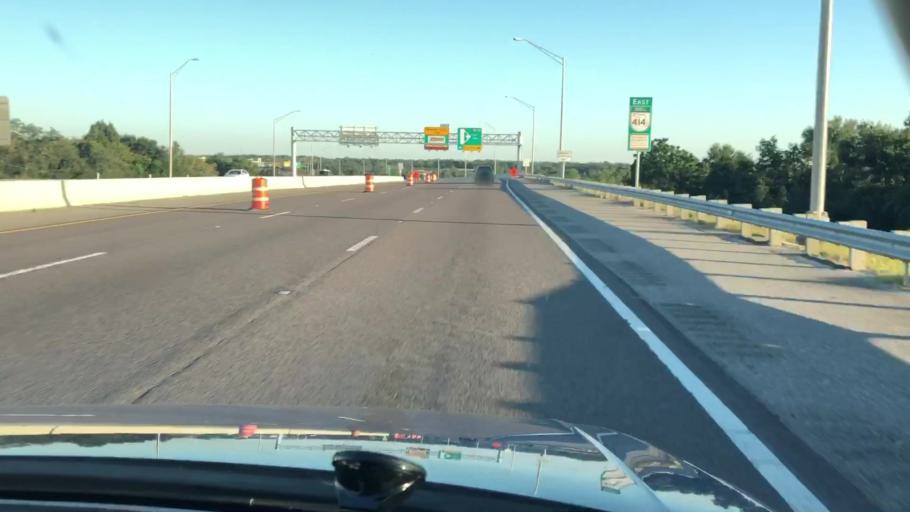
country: US
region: Florida
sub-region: Orange County
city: South Apopka
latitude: 28.6488
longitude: -81.5171
